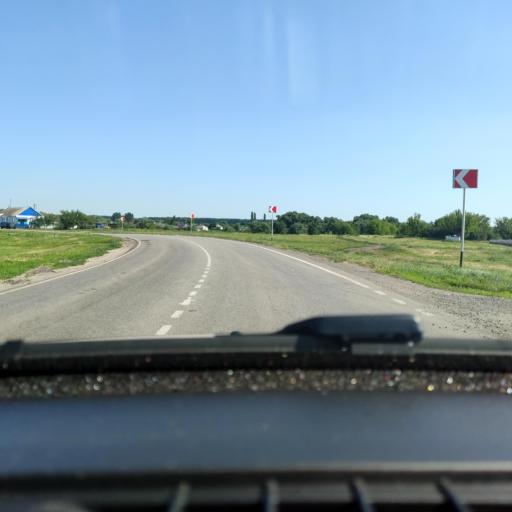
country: RU
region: Voronezj
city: Verkhnyaya Khava
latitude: 51.6743
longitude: 39.9422
